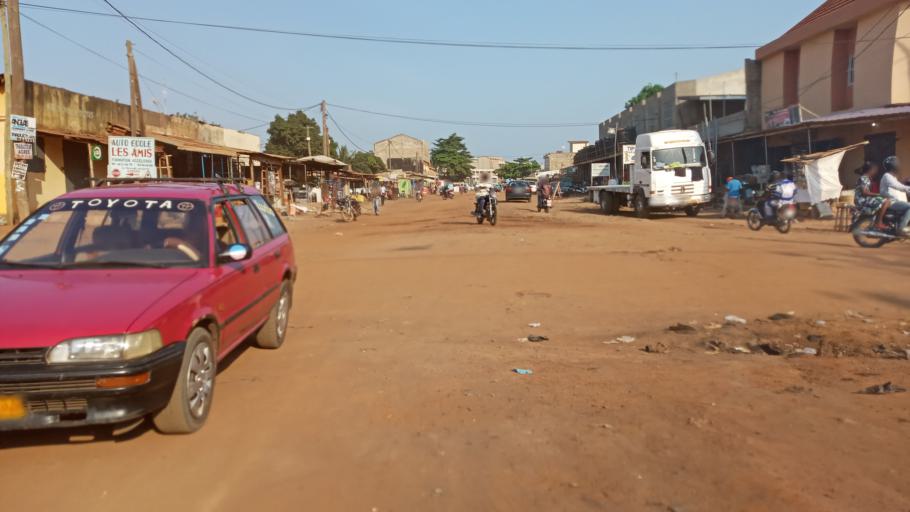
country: TG
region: Maritime
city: Lome
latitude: 6.1813
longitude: 1.1680
